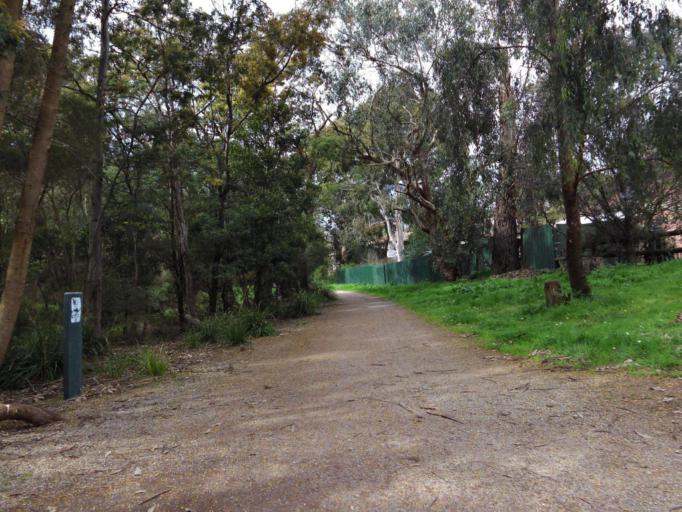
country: AU
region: Victoria
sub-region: Maroondah
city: Ringwood East
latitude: -37.8062
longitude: 145.2384
